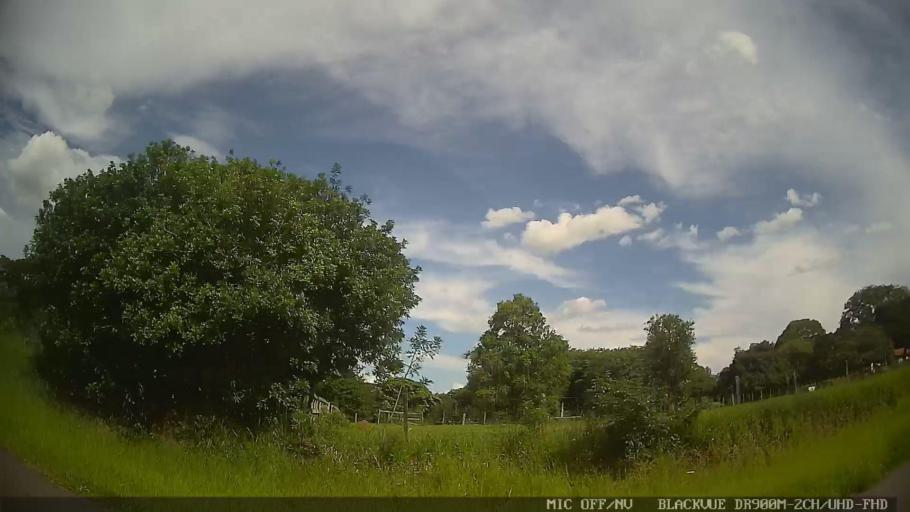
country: BR
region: Sao Paulo
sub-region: Conchas
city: Conchas
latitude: -23.0661
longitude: -47.9734
